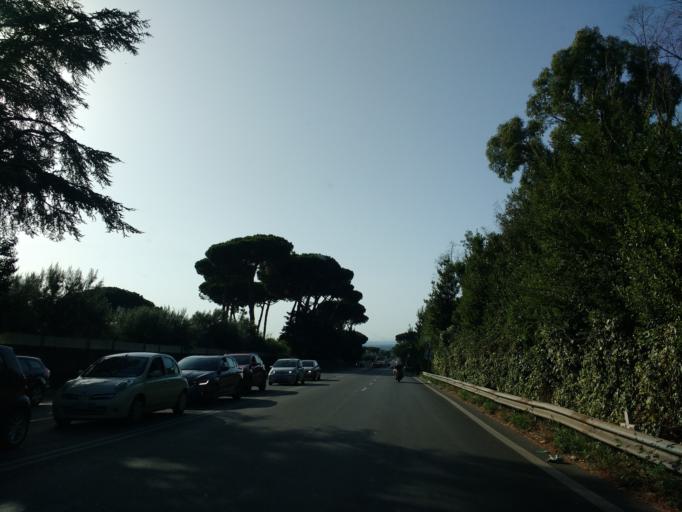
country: IT
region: Latium
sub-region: Citta metropolitana di Roma Capitale
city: Marino
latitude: 41.7560
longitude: 12.6285
